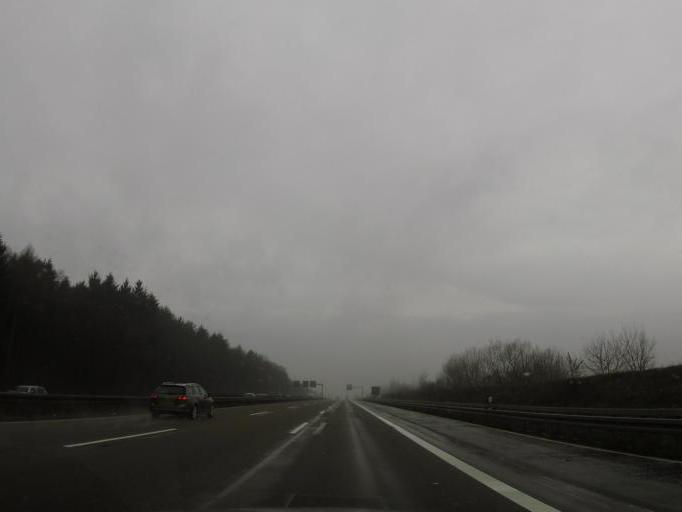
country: DE
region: Rheinland-Pfalz
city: Hambach
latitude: 50.4127
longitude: 7.9692
